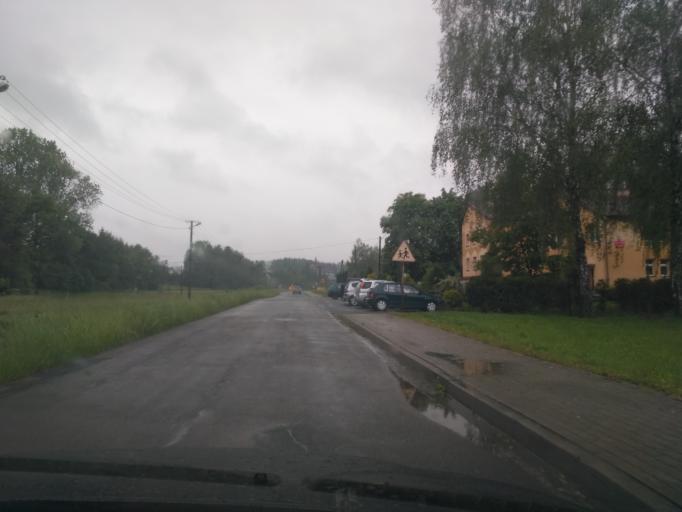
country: PL
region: Subcarpathian Voivodeship
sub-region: Powiat krosnienski
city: Leki
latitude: 49.7917
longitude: 21.6531
